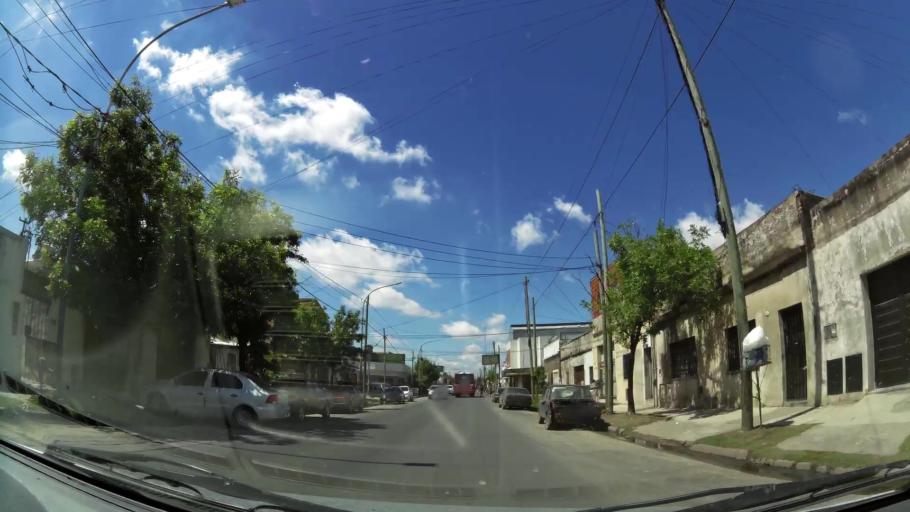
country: AR
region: Buenos Aires
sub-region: Partido de Lanus
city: Lanus
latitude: -34.6943
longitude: -58.4239
